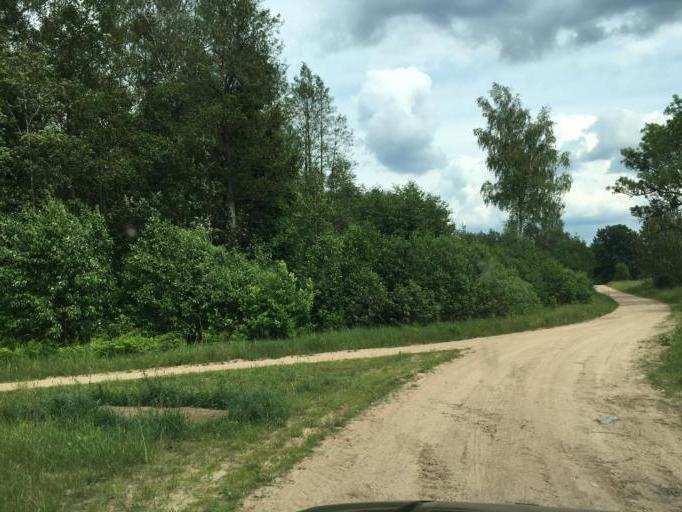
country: LV
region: Rugaju
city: Rugaji
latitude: 56.9761
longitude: 27.0516
